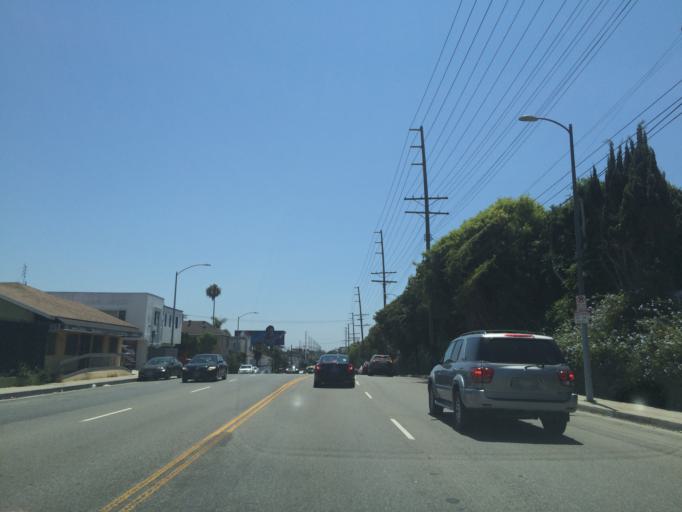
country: US
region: California
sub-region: Los Angeles County
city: Culver City
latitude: 34.0434
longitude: -118.3871
